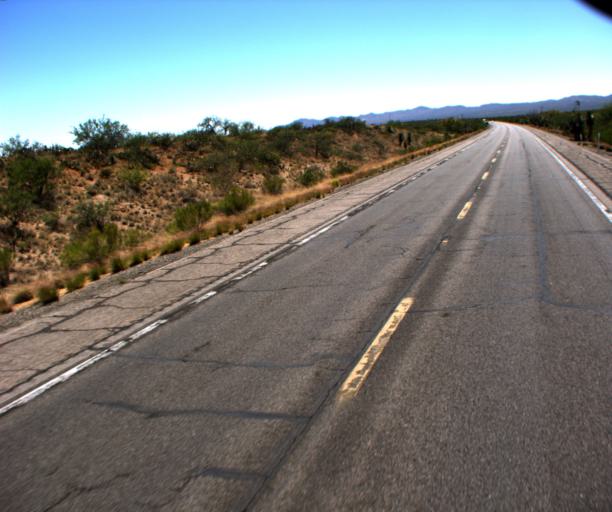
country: US
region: Arizona
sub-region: Pinal County
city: Oracle
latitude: 32.6117
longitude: -110.8422
